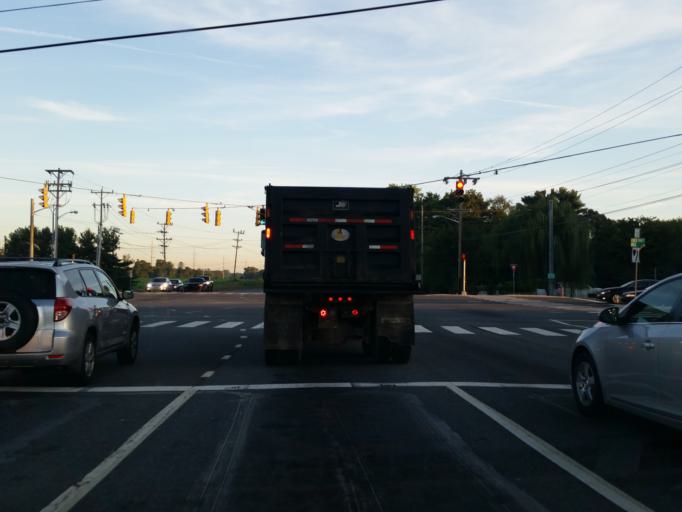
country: US
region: Delaware
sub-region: New Castle County
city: Brookside
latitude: 39.6612
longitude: -75.7360
